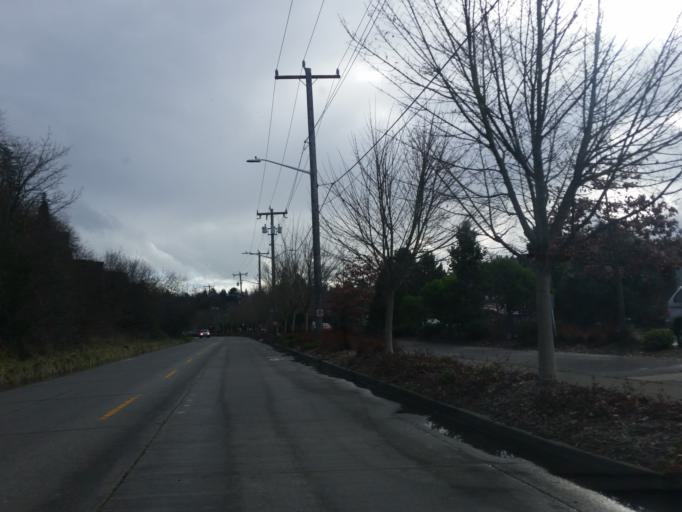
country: US
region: Washington
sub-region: King County
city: Seattle
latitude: 47.6713
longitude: -122.4050
